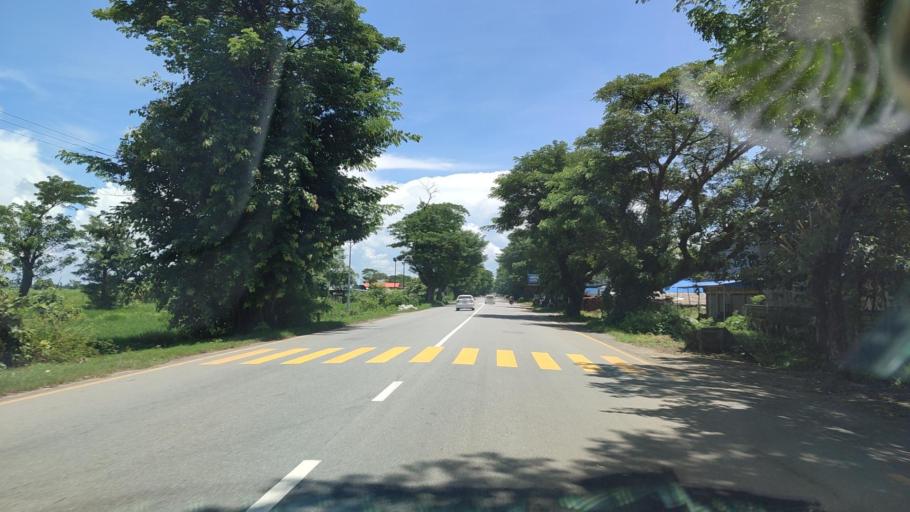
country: MM
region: Bago
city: Pyu
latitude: 18.2676
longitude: 96.5257
